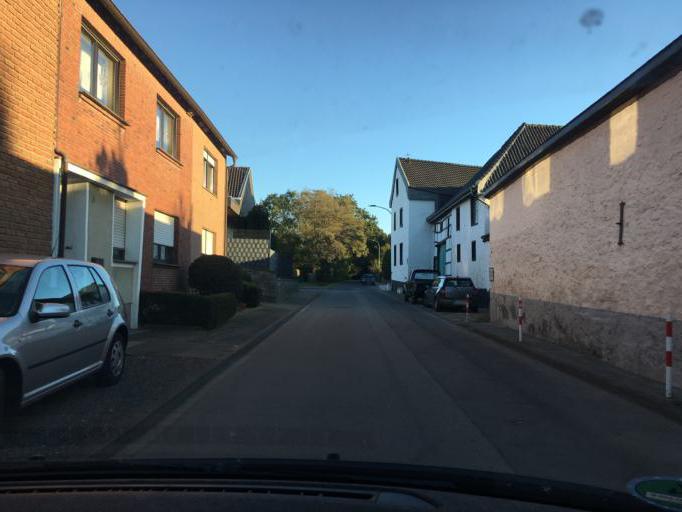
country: DE
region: North Rhine-Westphalia
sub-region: Regierungsbezirk Koln
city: Langerwehe
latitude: 50.7966
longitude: 6.3875
